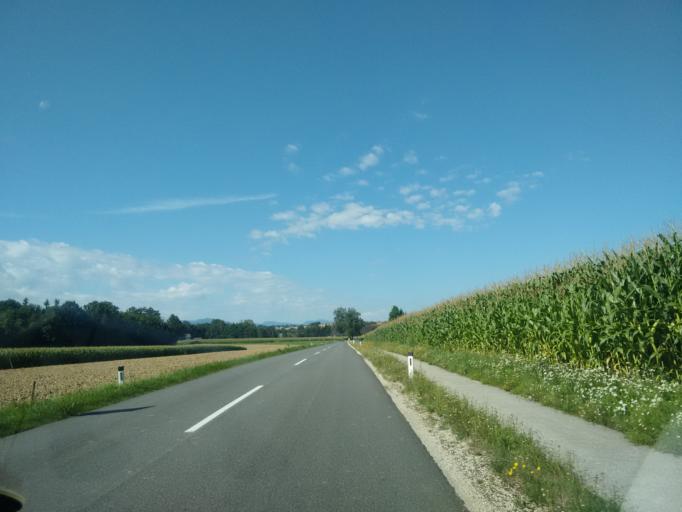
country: AT
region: Upper Austria
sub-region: Politischer Bezirk Steyr-Land
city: Pfarrkirchen bei Bad Hall
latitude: 48.0221
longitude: 14.1922
